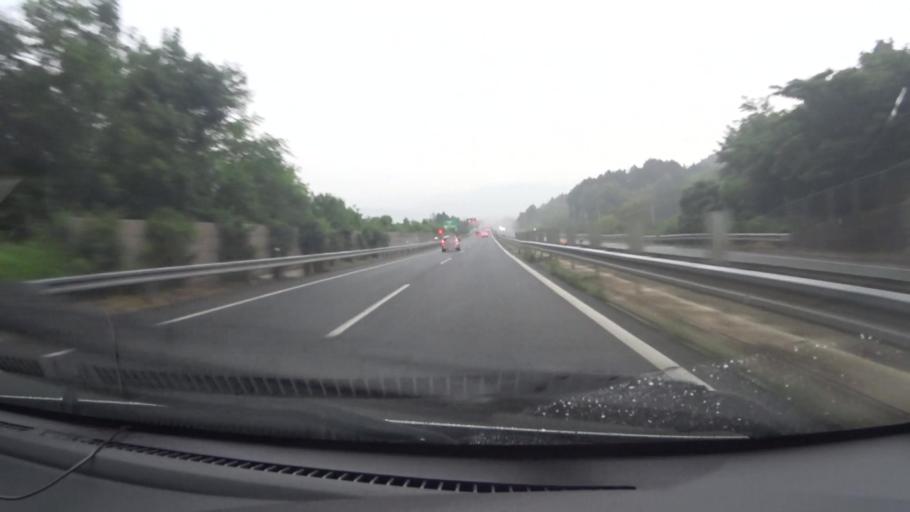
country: JP
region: Kyoto
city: Kameoka
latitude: 35.0394
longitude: 135.5403
